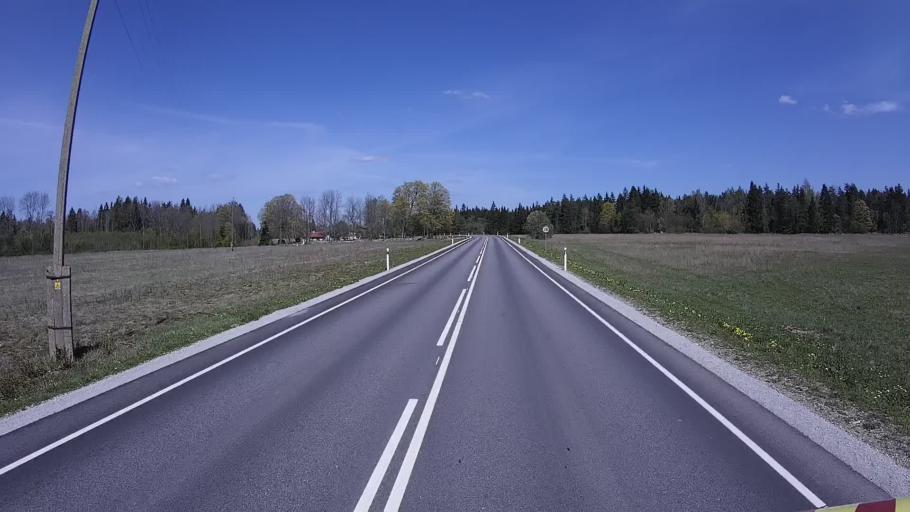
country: EE
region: Harju
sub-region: Paldiski linn
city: Paldiski
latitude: 59.1967
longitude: 24.0958
